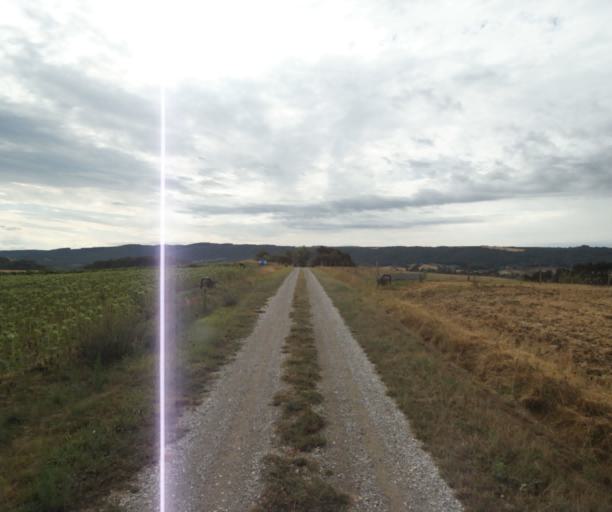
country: FR
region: Midi-Pyrenees
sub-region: Departement de la Haute-Garonne
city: Revel
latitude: 43.4271
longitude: 1.9672
